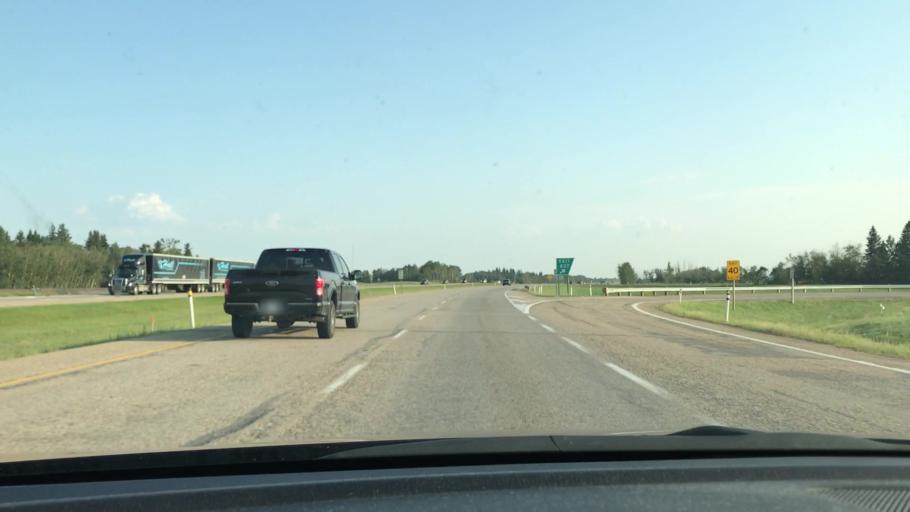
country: CA
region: Alberta
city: Lacombe
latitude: 52.5563
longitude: -113.6630
